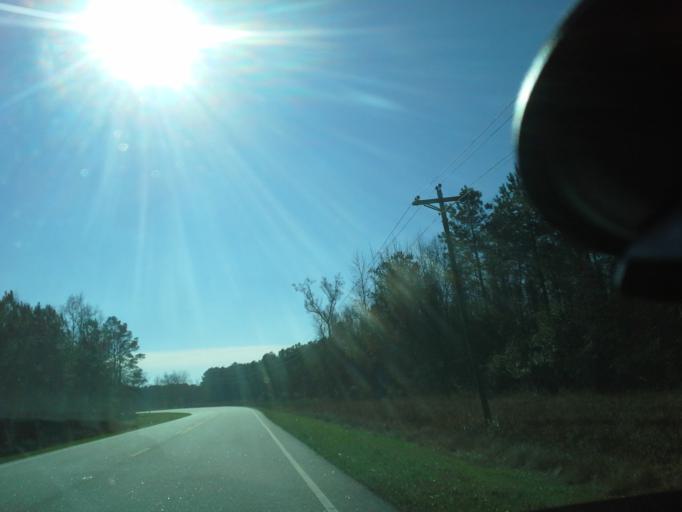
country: US
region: North Carolina
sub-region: Beaufort County
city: Belhaven
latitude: 35.5530
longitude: -76.7035
